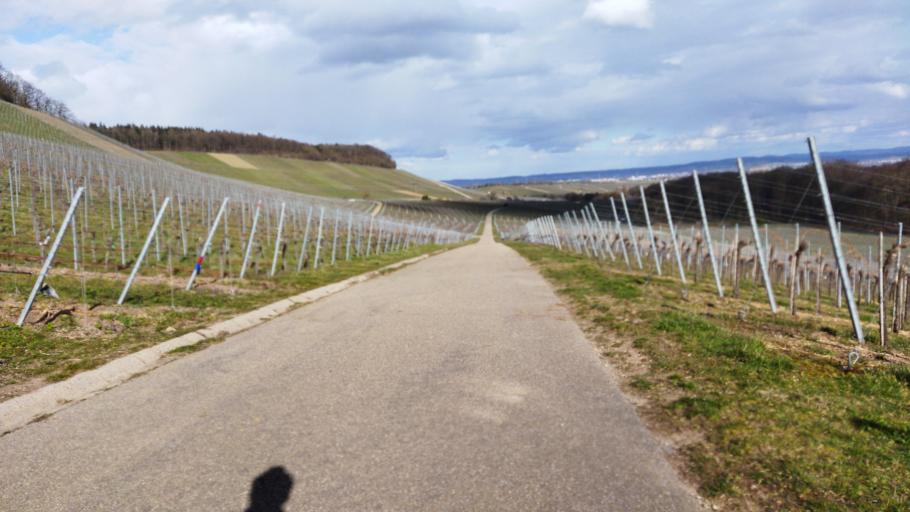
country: DE
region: Baden-Wuerttemberg
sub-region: Regierungsbezirk Stuttgart
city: Schwaigern
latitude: 49.1189
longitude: 9.0848
